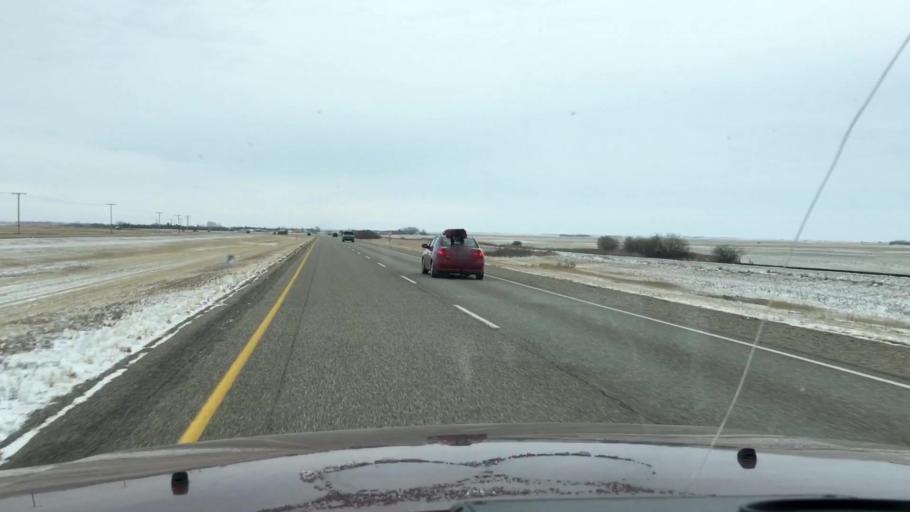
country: CA
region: Saskatchewan
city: Watrous
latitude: 51.1759
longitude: -105.9352
